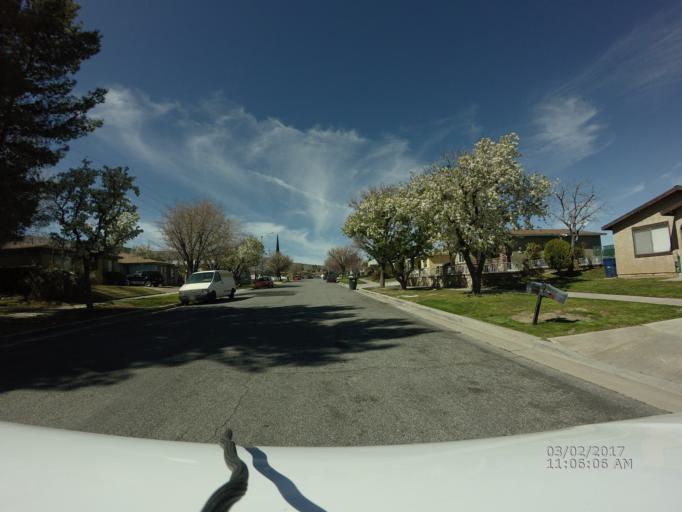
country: US
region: California
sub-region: Los Angeles County
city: Quartz Hill
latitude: 34.6461
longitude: -118.2515
